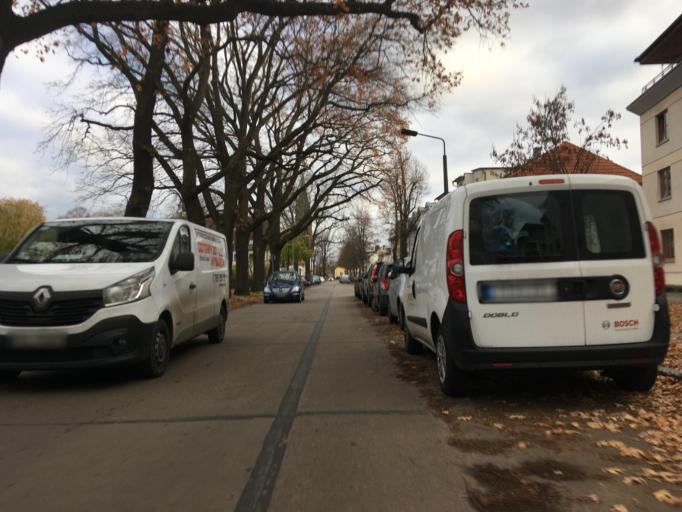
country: DE
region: Berlin
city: Altglienicke
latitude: 52.4223
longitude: 13.5357
